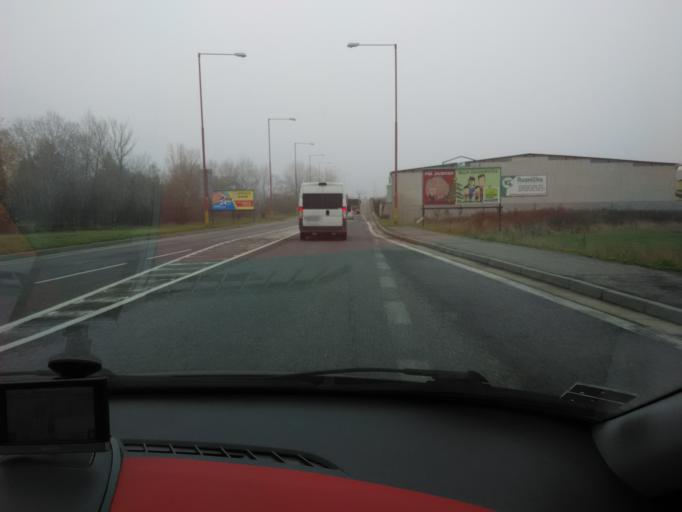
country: AT
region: Burgenland
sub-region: Politischer Bezirk Neusiedl am See
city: Kittsee
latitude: 48.1172
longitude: 17.0848
